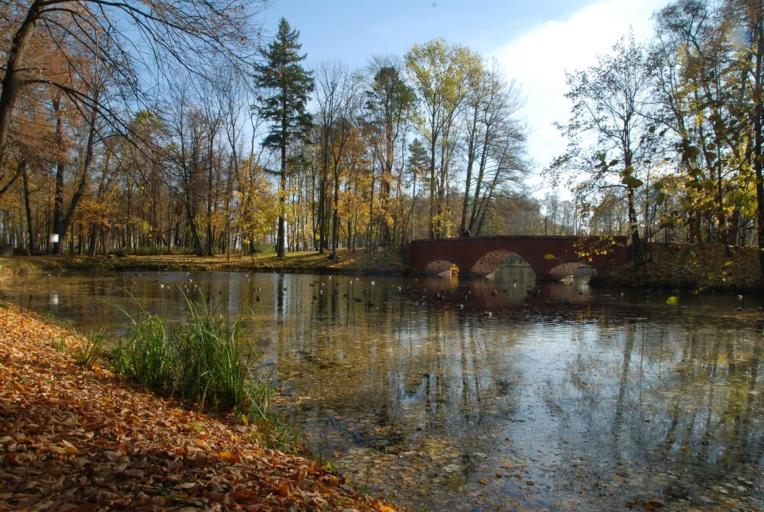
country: PL
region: Masovian Voivodeship
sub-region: Powiat pruszkowski
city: Nadarzyn
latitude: 52.0455
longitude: 20.7803
